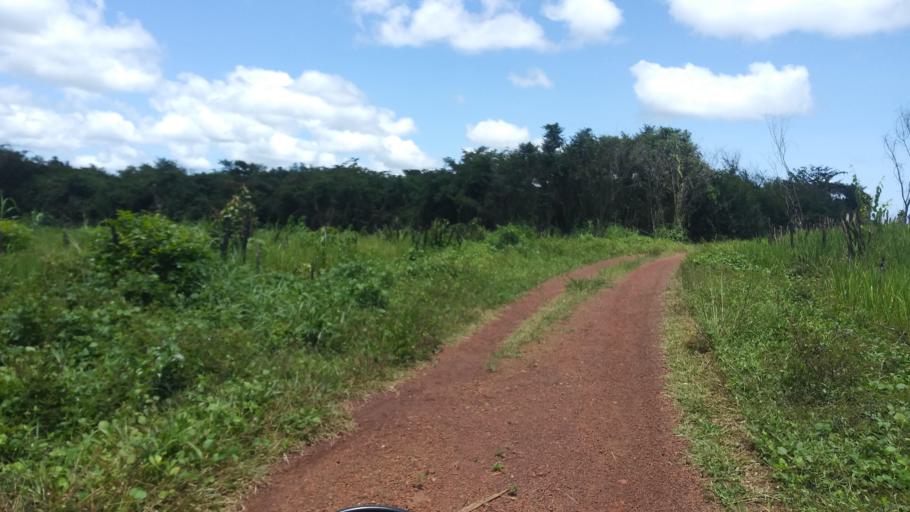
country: SL
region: Northern Province
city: Binkolo
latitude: 8.9075
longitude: -11.9850
